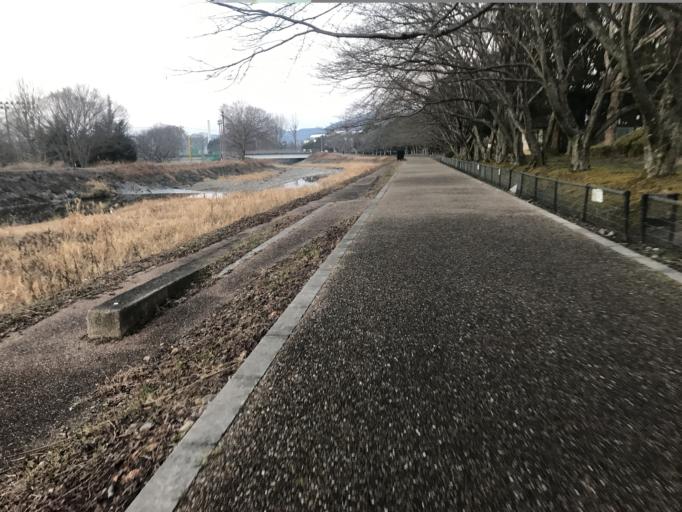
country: JP
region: Kyoto
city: Kameoka
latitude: 35.0109
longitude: 135.5492
